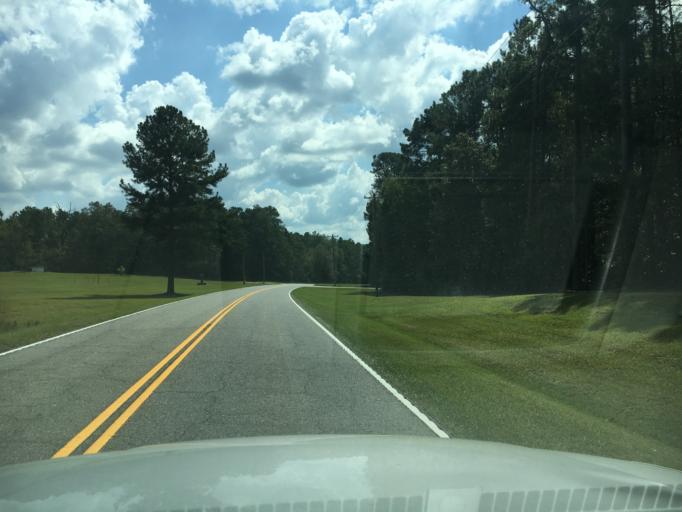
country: US
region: South Carolina
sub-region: Greenwood County
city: Greenwood
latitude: 34.1009
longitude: -82.1290
